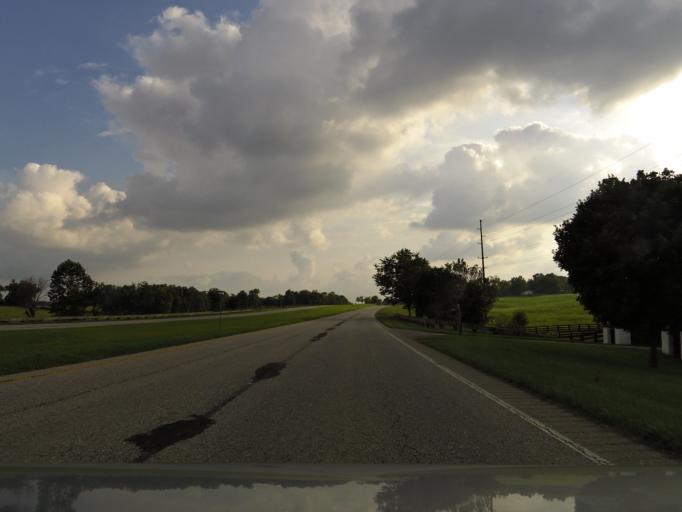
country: US
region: Kentucky
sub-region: Bourbon County
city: Paris
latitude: 38.1389
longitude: -84.3602
